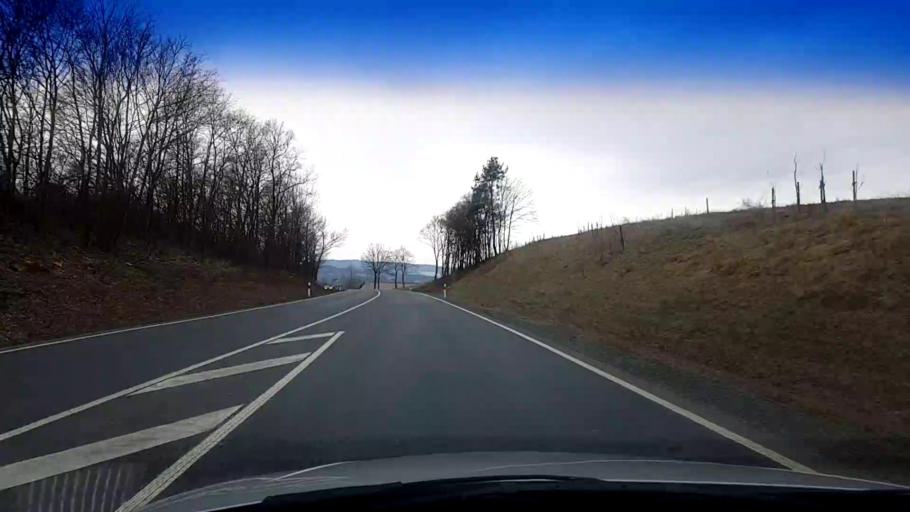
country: DE
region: Bavaria
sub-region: Upper Franconia
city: Kulmbach
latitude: 50.0848
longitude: 11.4614
